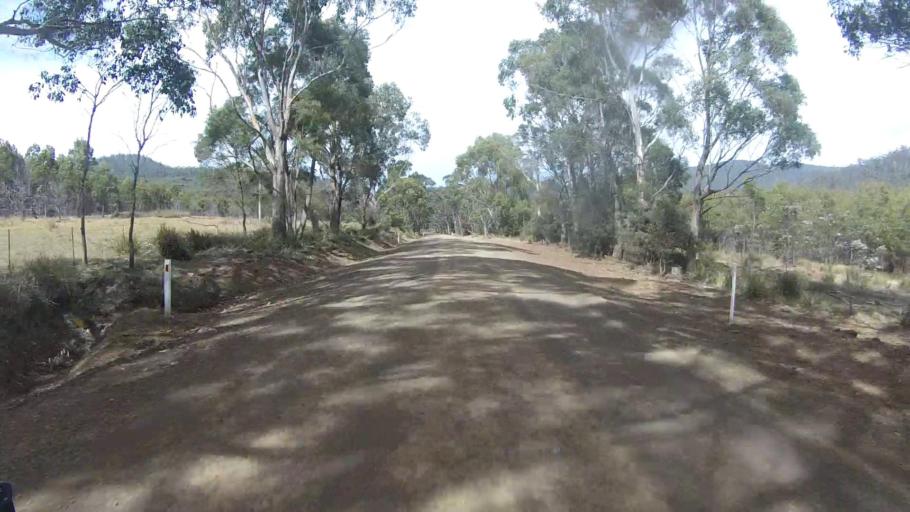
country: AU
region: Tasmania
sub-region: Sorell
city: Sorell
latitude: -42.6607
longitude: 147.8948
